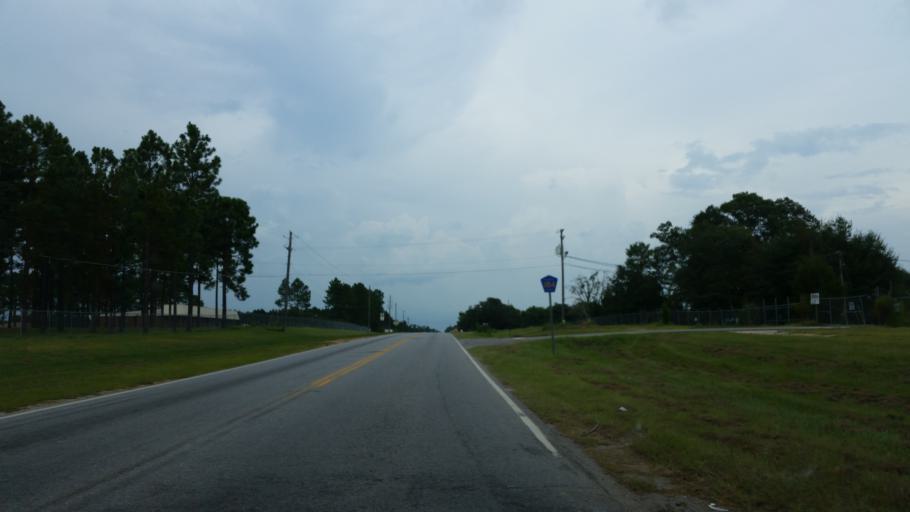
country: US
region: Florida
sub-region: Escambia County
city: Cantonment
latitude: 30.6505
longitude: -87.3210
